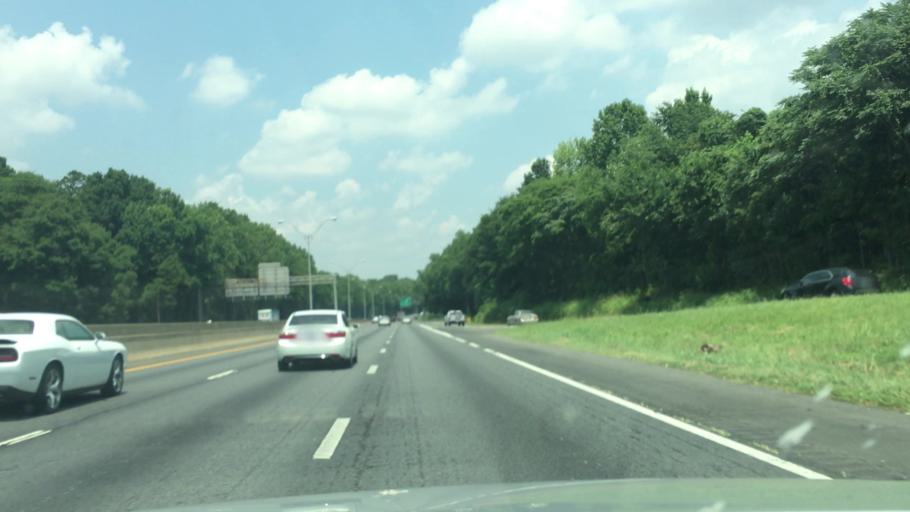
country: US
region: North Carolina
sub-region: Mecklenburg County
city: Charlotte
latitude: 35.1991
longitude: -80.8820
